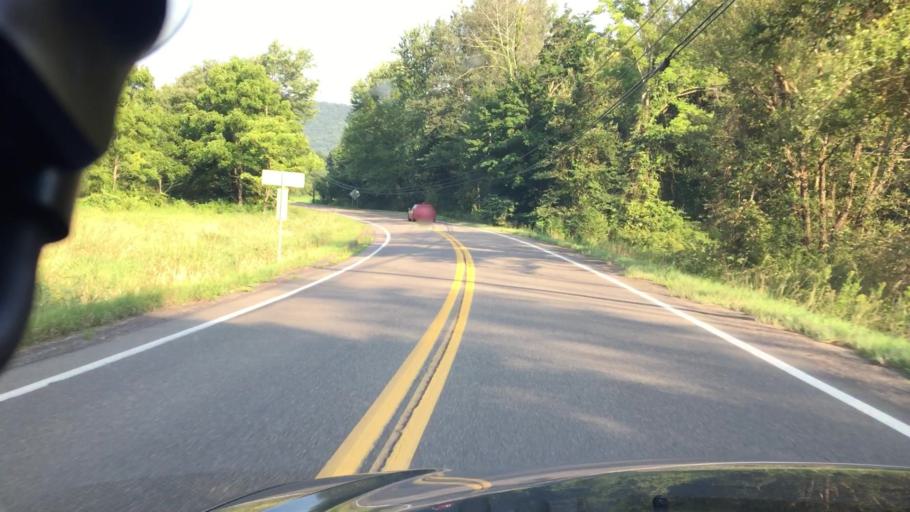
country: US
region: Pennsylvania
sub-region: Columbia County
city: Espy
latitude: 40.9816
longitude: -76.3876
